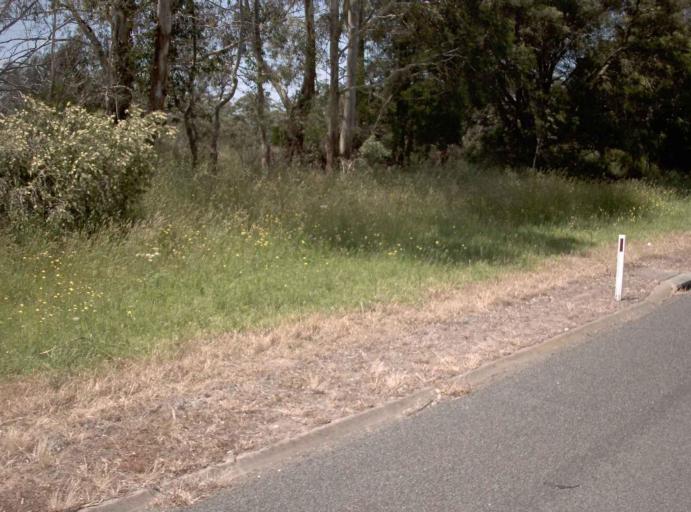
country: AU
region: Victoria
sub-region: Baw Baw
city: Warragul
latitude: -38.1059
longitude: 145.8568
